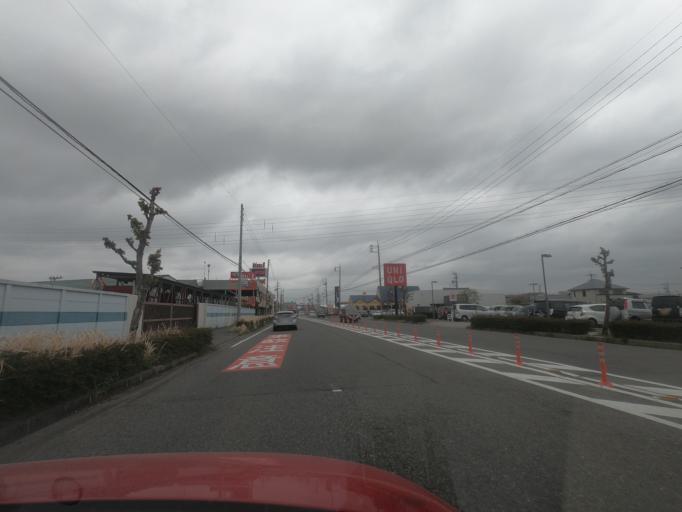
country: JP
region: Aichi
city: Kasugai
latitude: 35.2619
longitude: 136.9658
